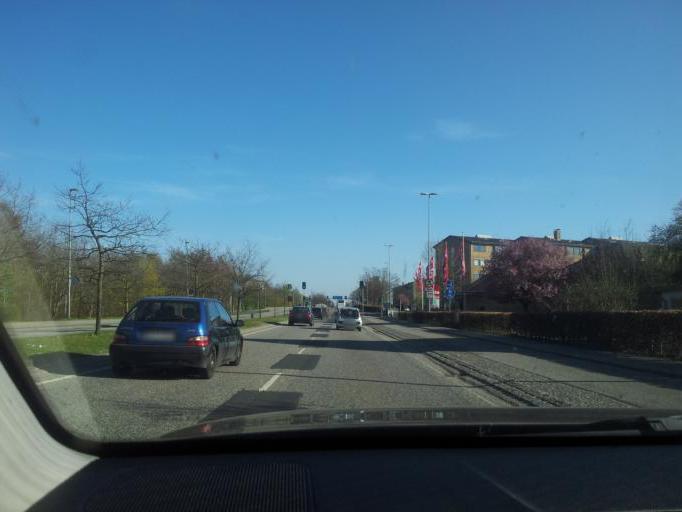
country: DK
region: South Denmark
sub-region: Odense Kommune
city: Neder Holluf
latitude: 55.3903
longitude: 10.4238
